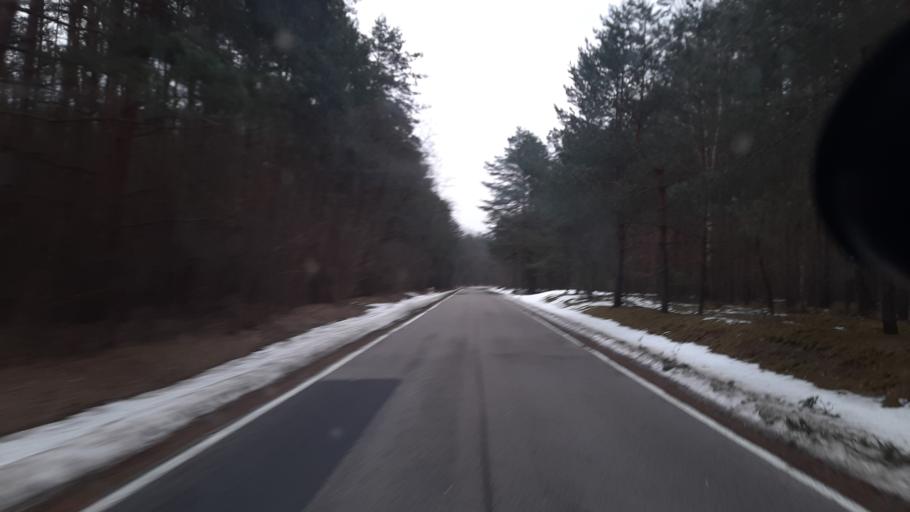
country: PL
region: Lublin Voivodeship
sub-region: Powiat wlodawski
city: Wlodawa
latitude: 51.4905
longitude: 23.6046
